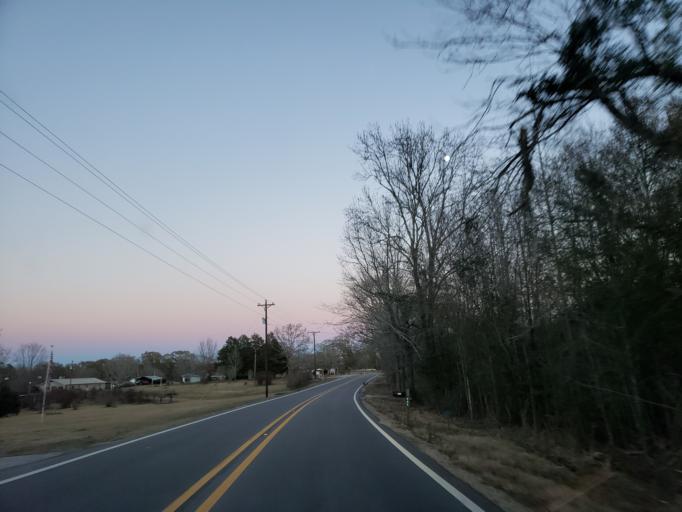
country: US
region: Mississippi
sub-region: Jones County
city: Ellisville
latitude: 31.5816
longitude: -89.2476
